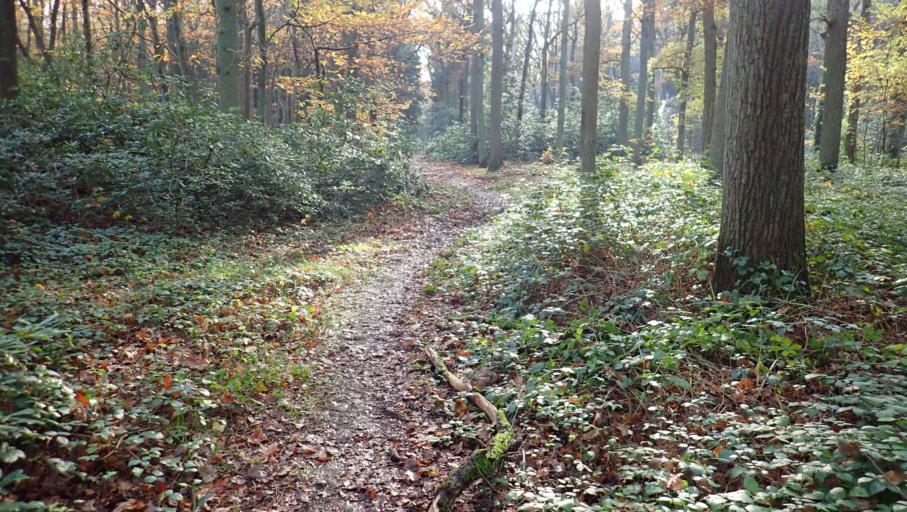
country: BE
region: Flanders
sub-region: Provincie Antwerpen
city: Kalmthout
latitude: 51.3500
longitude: 4.5219
